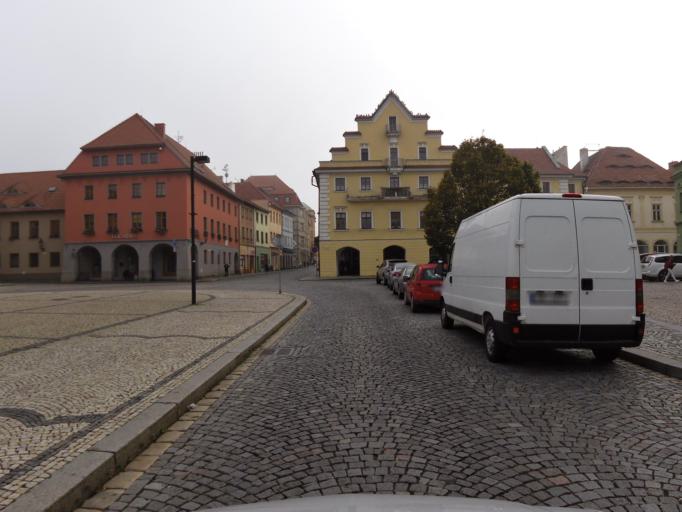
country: CZ
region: Ustecky
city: Zatec
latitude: 50.3288
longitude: 13.5446
